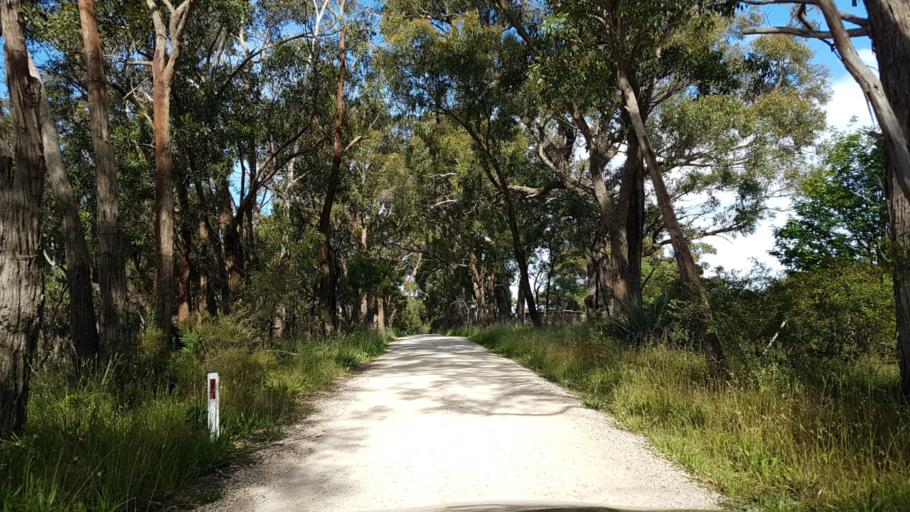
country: AU
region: South Australia
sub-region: Adelaide Hills
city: Adelaide Hills
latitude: -34.9050
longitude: 138.7421
